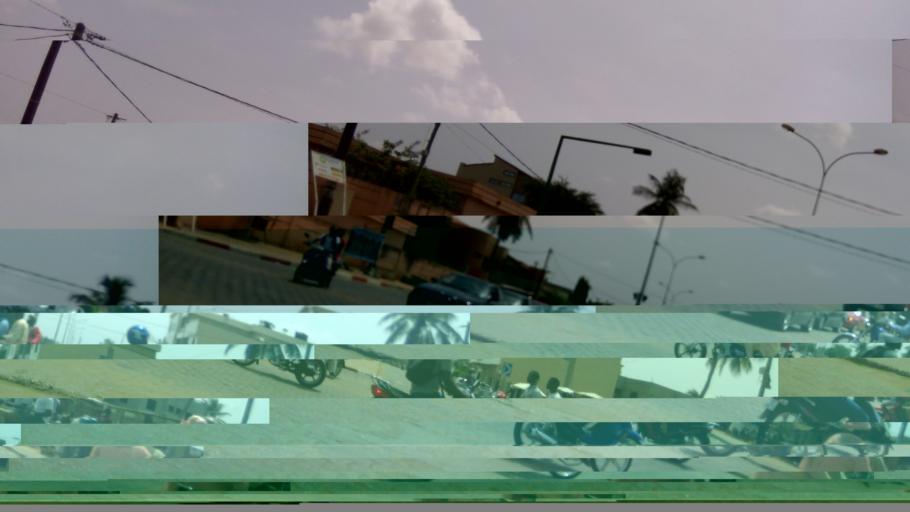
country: TG
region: Maritime
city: Lome
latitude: 6.1872
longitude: 1.1929
